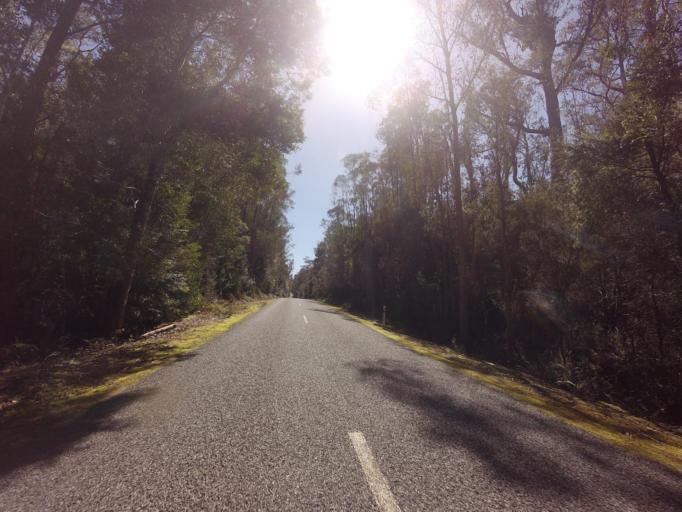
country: AU
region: Tasmania
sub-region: Derwent Valley
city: New Norfolk
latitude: -42.7509
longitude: 146.4118
